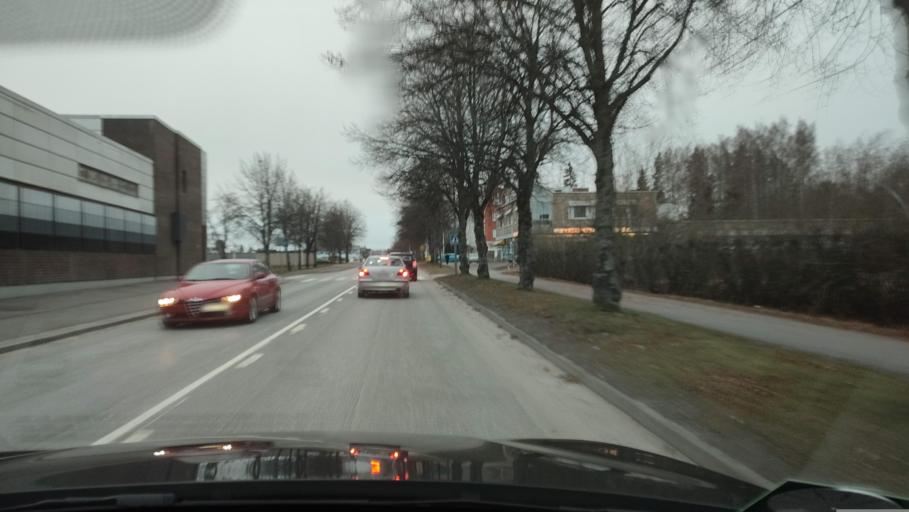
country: FI
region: Southern Ostrobothnia
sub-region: Suupohja
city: Kauhajoki
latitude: 62.4276
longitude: 22.1777
